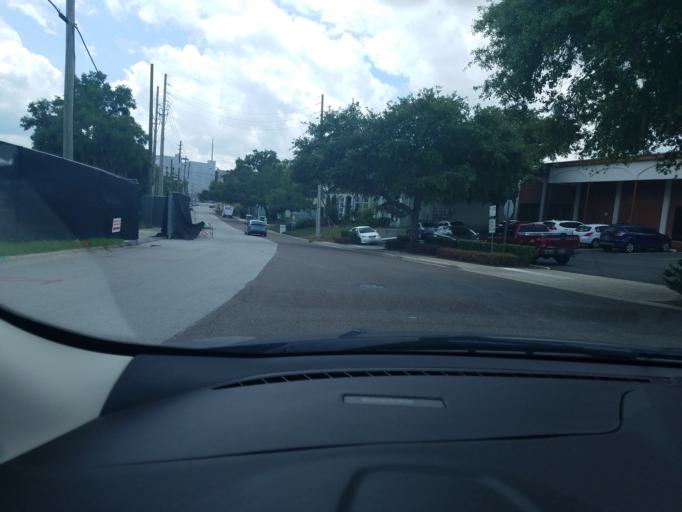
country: US
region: Florida
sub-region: Orange County
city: Fairview Shores
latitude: 28.5702
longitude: -81.3714
